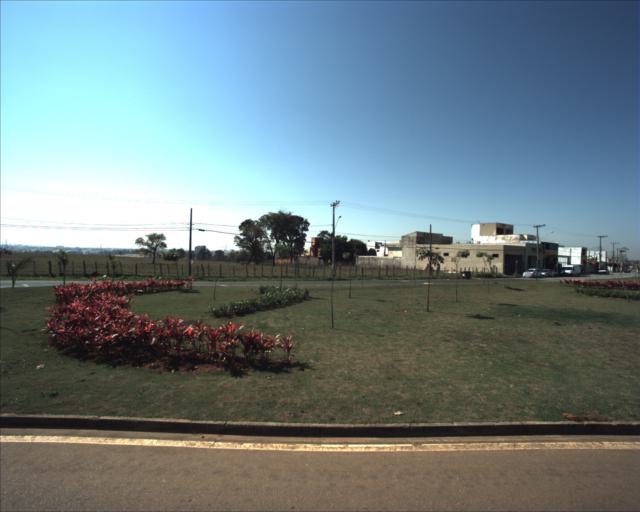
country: BR
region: Sao Paulo
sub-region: Sorocaba
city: Sorocaba
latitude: -23.4935
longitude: -47.5317
